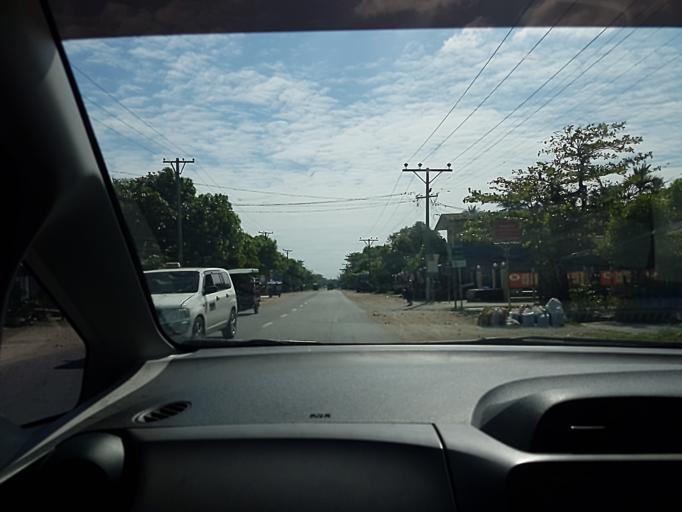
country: MM
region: Mon
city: Thaton
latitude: 16.6965
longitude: 97.4252
